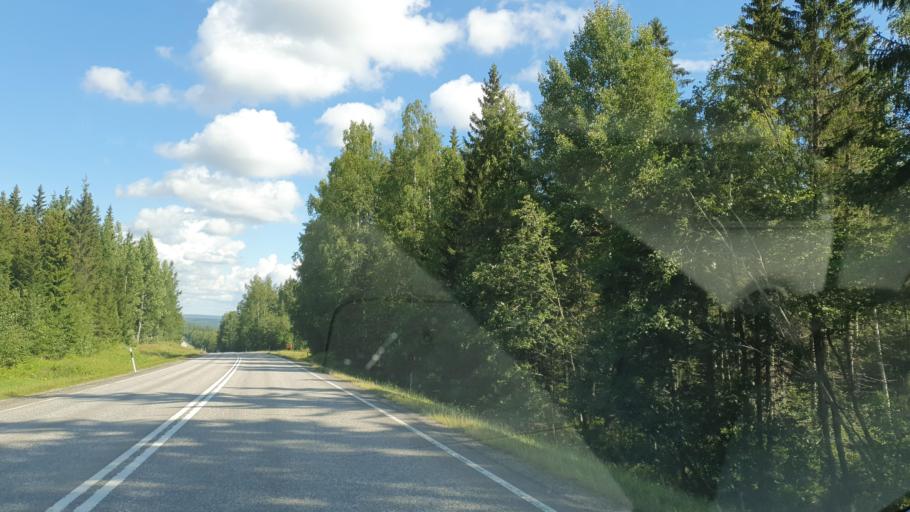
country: FI
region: Northern Savo
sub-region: Ylae-Savo
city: Sonkajaervi
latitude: 63.6845
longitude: 27.3387
